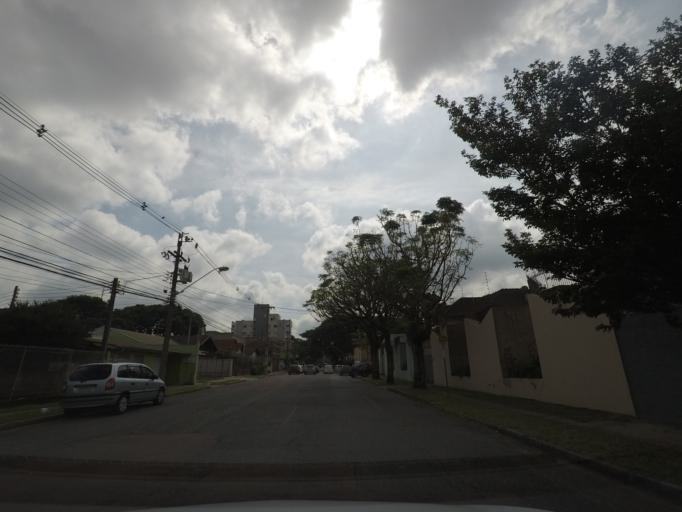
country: BR
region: Parana
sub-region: Curitiba
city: Curitiba
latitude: -25.4512
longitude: -49.2553
